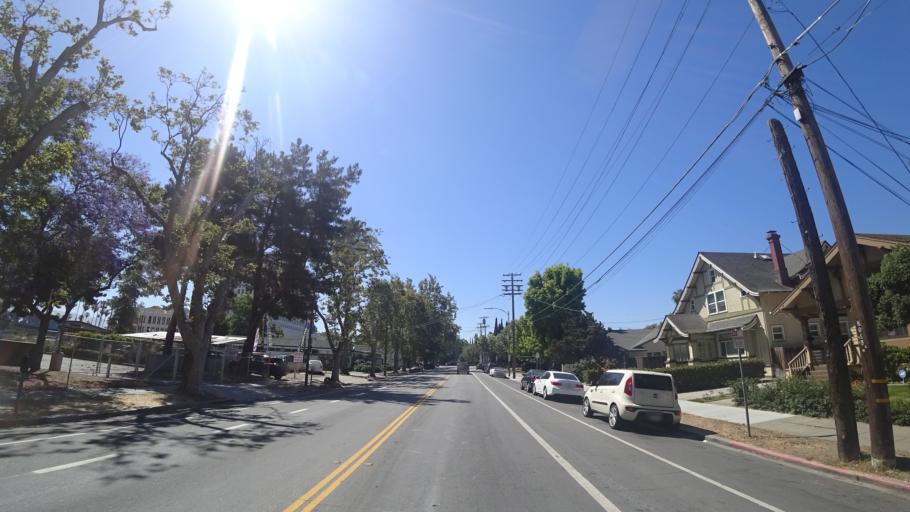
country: US
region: California
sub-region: Santa Clara County
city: San Jose
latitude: 37.3435
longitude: -121.8792
